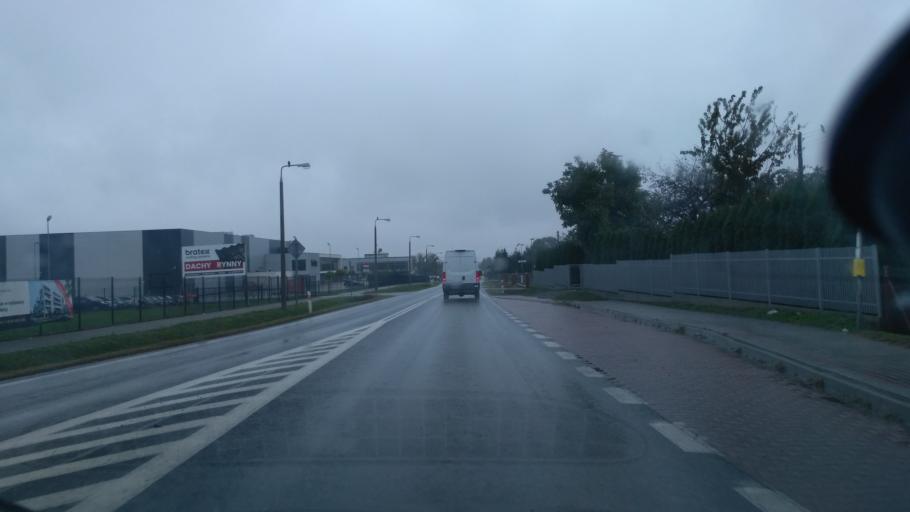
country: PL
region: Subcarpathian Voivodeship
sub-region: Powiat debicki
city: Debica
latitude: 50.0587
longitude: 21.4456
